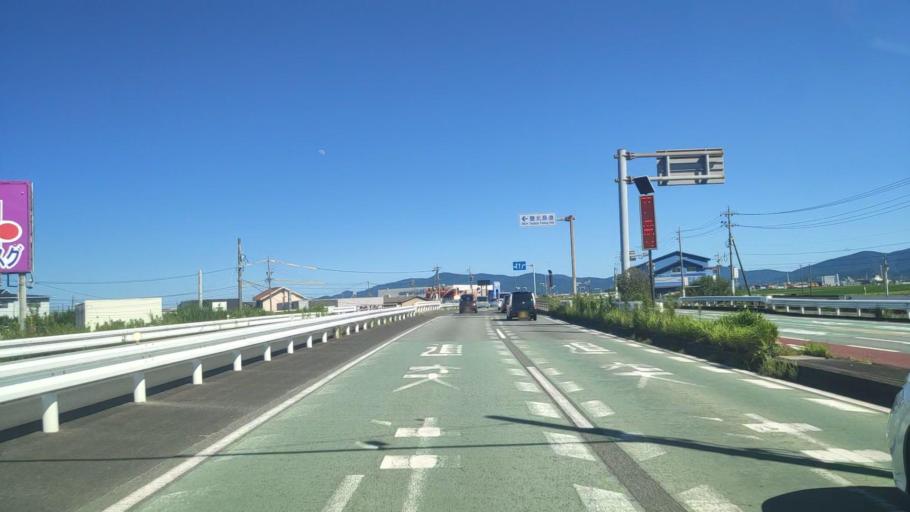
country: JP
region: Mie
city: Ise
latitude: 34.5340
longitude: 136.6799
